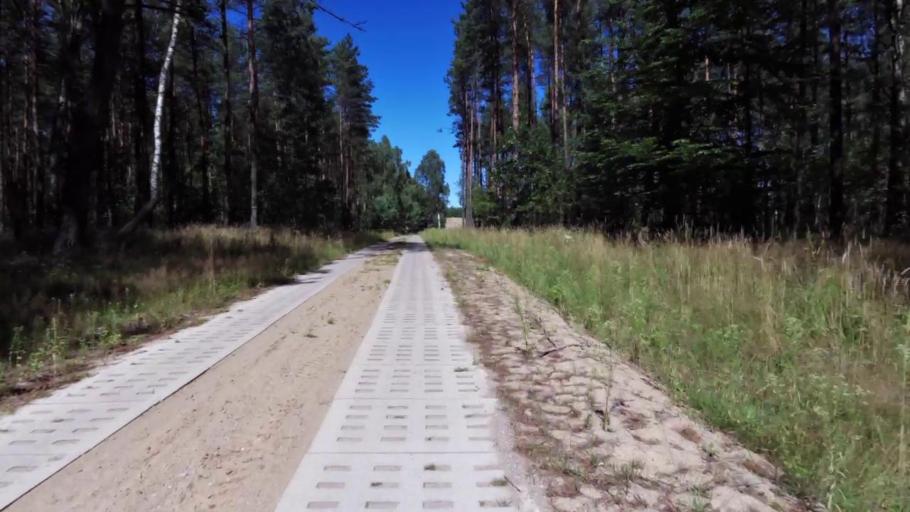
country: PL
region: West Pomeranian Voivodeship
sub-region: Powiat szczecinecki
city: Szczecinek
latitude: 53.6277
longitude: 16.6610
